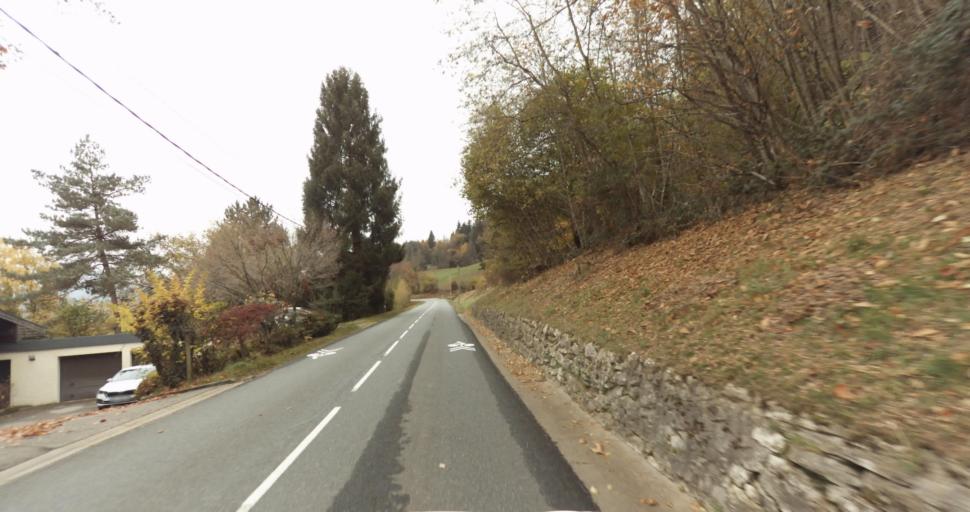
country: FR
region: Rhone-Alpes
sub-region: Departement de la Haute-Savoie
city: Sevrier
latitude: 45.8398
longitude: 6.1399
